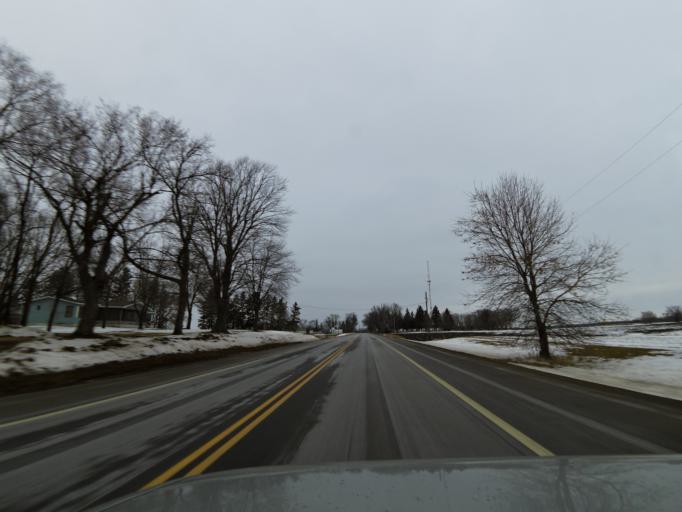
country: US
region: Wisconsin
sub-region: Pierce County
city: Prescott
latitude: 44.8241
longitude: -92.8001
